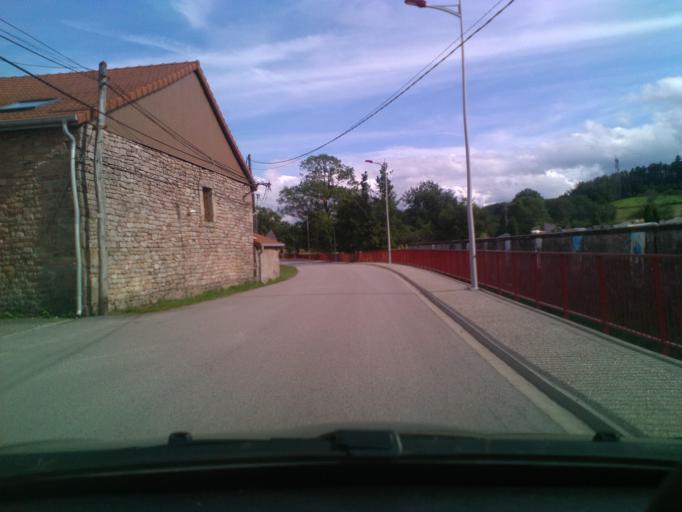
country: FR
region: Lorraine
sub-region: Departement des Vosges
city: Corcieux
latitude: 48.1952
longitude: 6.8541
